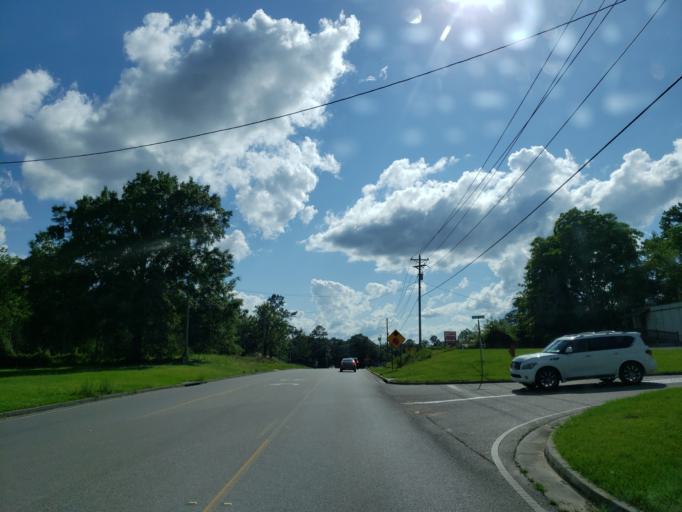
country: US
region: Mississippi
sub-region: Lamar County
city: Arnold Line
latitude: 31.3357
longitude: -89.3653
